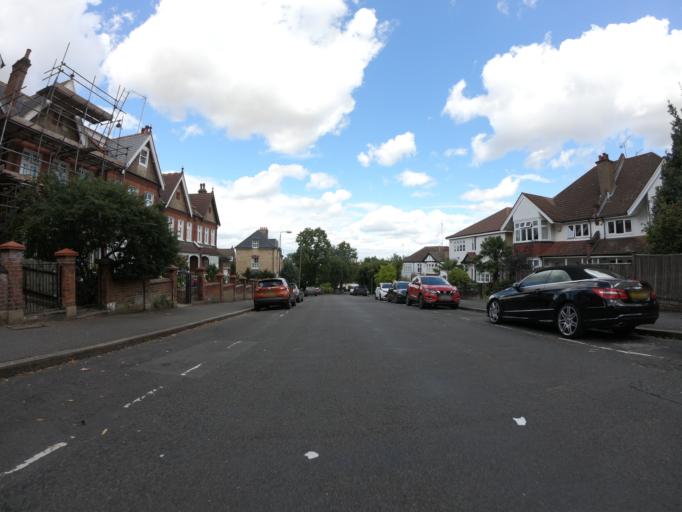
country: GB
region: England
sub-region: Greater London
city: Blackheath
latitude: 51.4824
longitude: 0.0164
